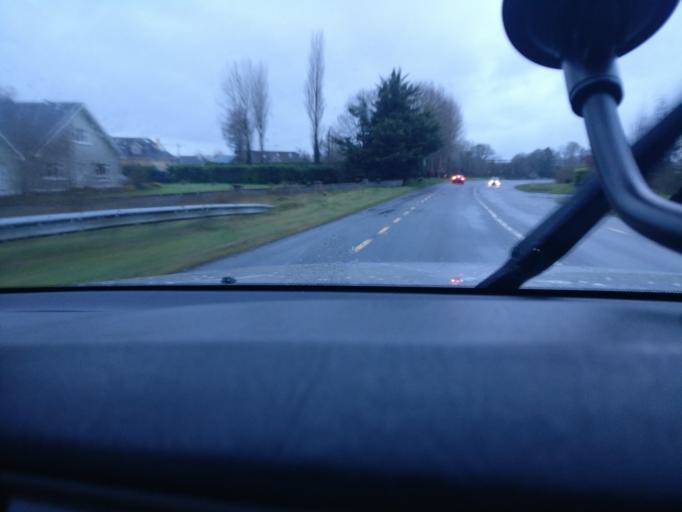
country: IE
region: Connaught
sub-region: County Galway
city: Ballinasloe
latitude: 53.3060
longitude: -8.2961
